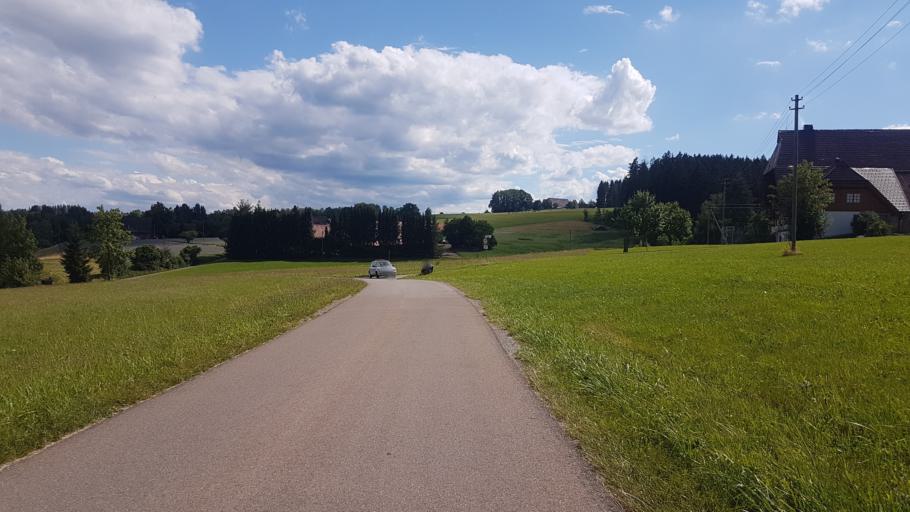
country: DE
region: Baden-Wuerttemberg
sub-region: Freiburg Region
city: Konigsfeld im Schwarzwald
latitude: 48.1536
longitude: 8.4075
